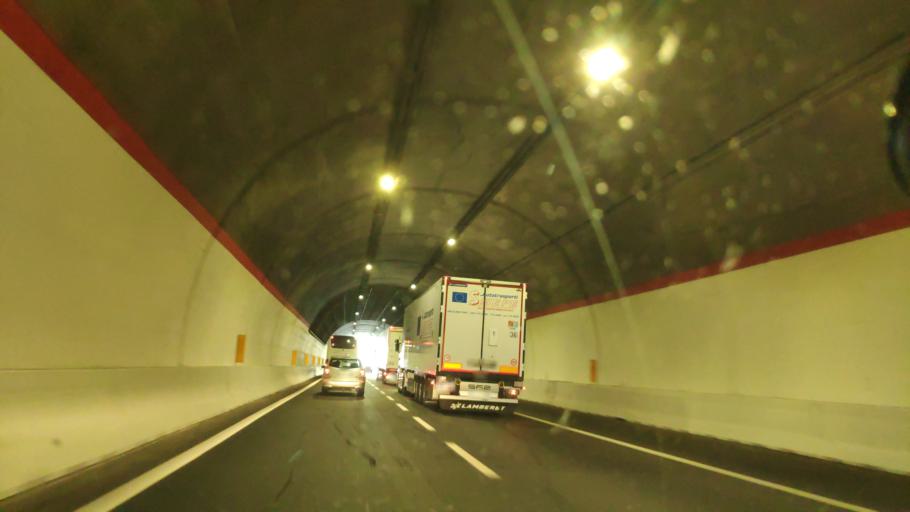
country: IT
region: Campania
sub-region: Provincia di Salerno
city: Pertosa
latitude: 40.5336
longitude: 15.4636
